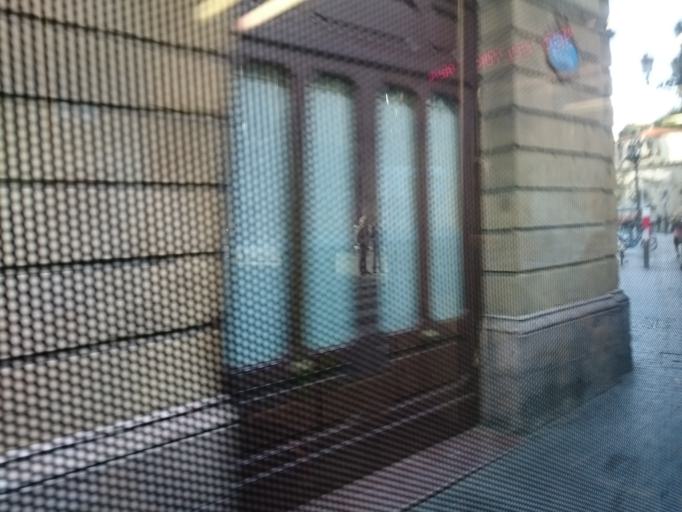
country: ES
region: Basque Country
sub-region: Bizkaia
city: Bilbao
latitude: 43.2593
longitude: -2.9248
